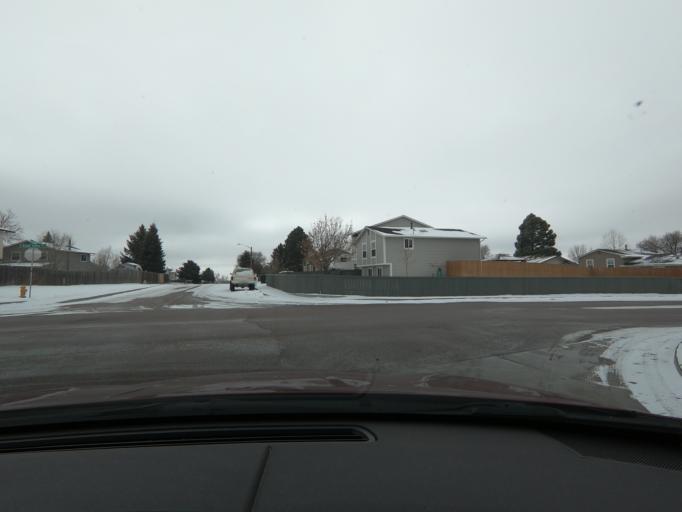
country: US
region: Colorado
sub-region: El Paso County
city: Security-Widefield
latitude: 38.7257
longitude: -104.6924
